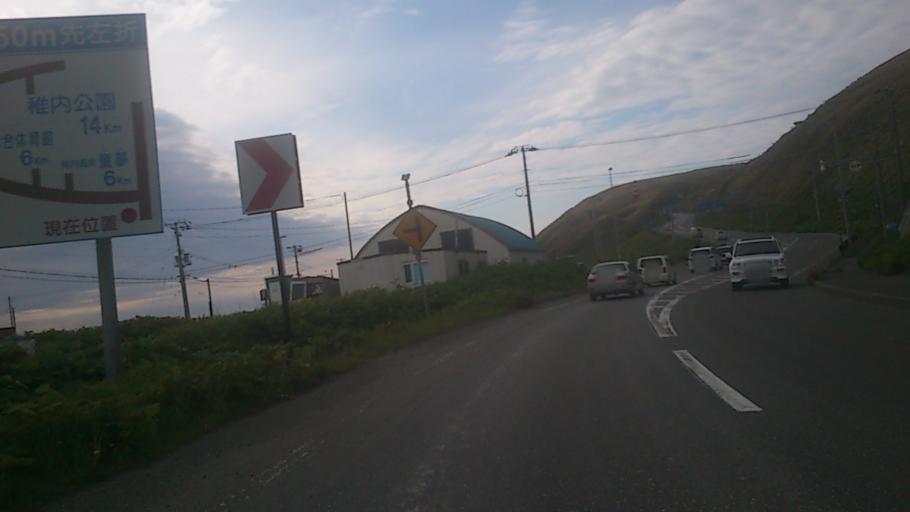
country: JP
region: Hokkaido
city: Wakkanai
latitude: 45.3734
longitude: 141.6564
